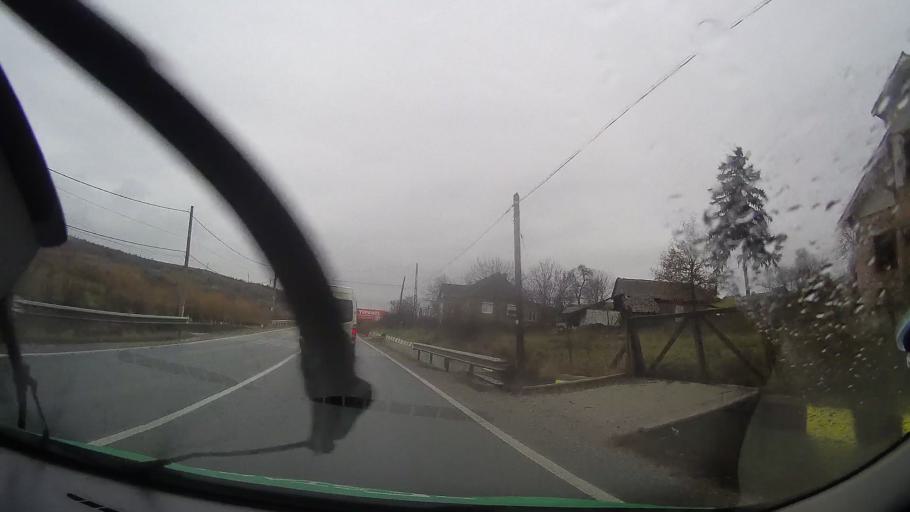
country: RO
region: Bistrita-Nasaud
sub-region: Comuna Galatii Bistritei
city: Galatii Bistritei
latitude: 47.0135
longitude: 24.4077
